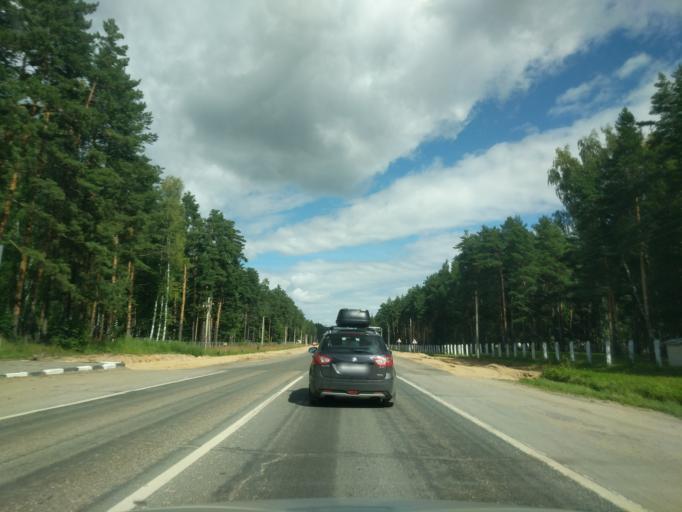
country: RU
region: Jaroslavl
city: Levashevo
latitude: 57.6755
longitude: 40.5876
